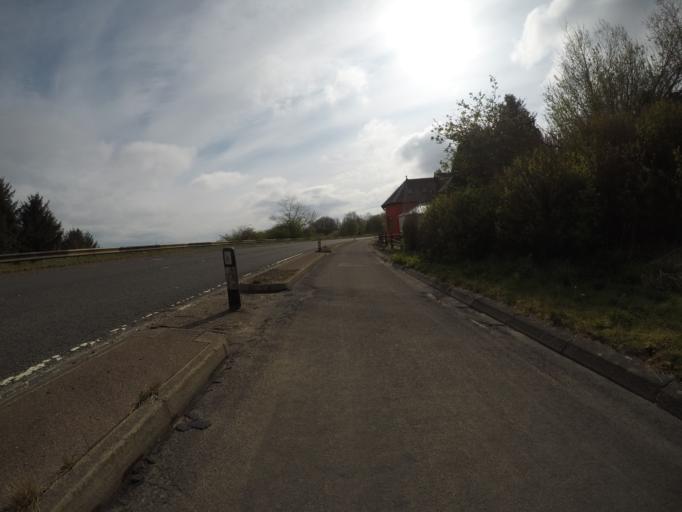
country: GB
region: Scotland
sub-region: East Renfrewshire
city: Newton Mearns
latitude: 55.7427
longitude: -4.3661
